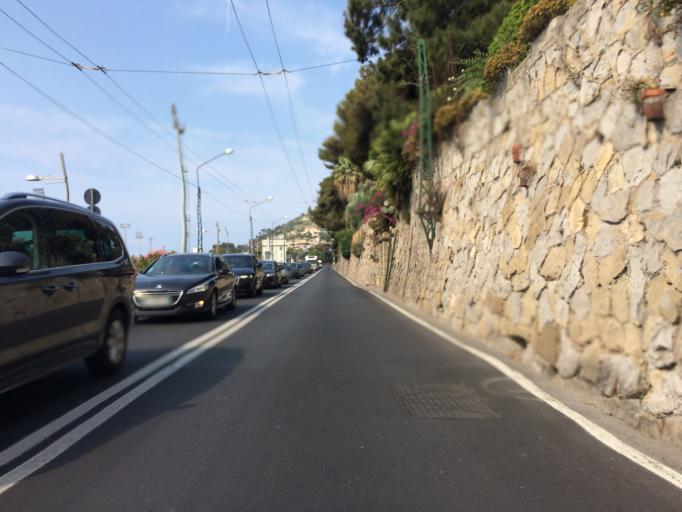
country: IT
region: Liguria
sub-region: Provincia di Imperia
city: San Remo
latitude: 43.8072
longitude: 7.7516
